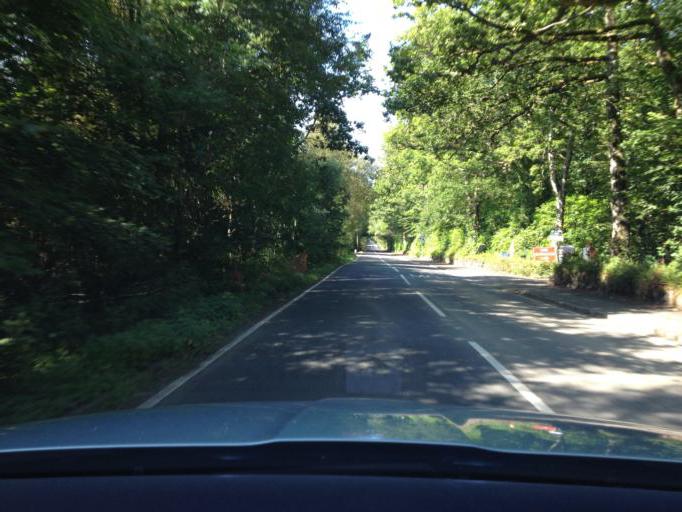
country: GB
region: Scotland
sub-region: West Dunbartonshire
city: Balloch
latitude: 56.0818
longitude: -4.5042
